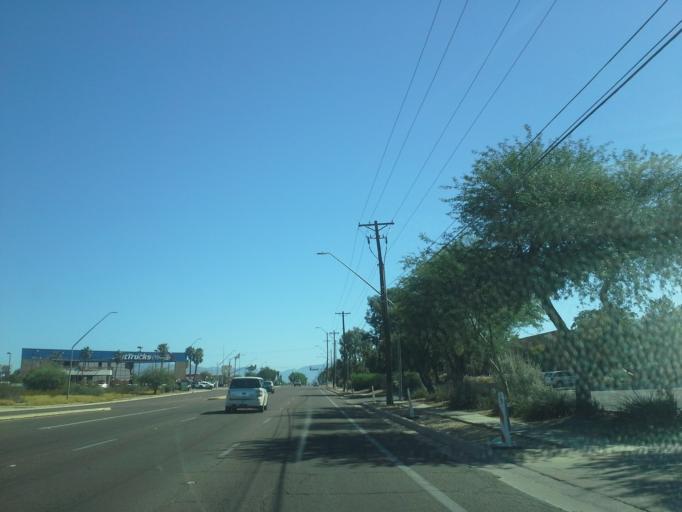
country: US
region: Arizona
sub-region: Pima County
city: Summit
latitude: 32.1340
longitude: -110.9289
